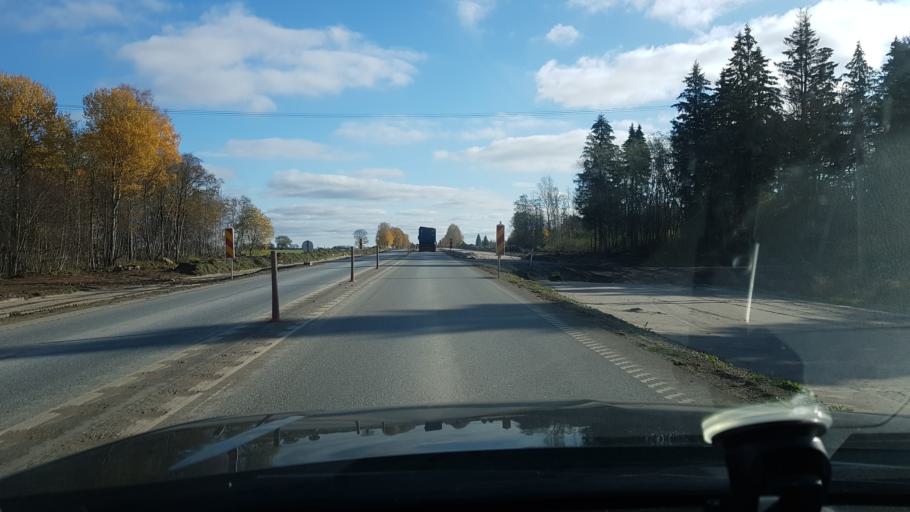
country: EE
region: Laeaene-Virumaa
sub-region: Haljala vald
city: Haljala
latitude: 59.4352
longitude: 26.1685
